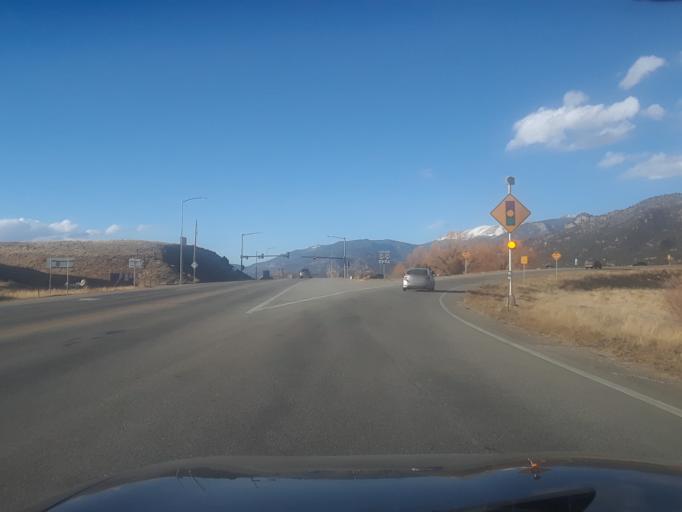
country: US
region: Colorado
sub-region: Chaffee County
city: Buena Vista
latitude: 38.8059
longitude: -106.1150
